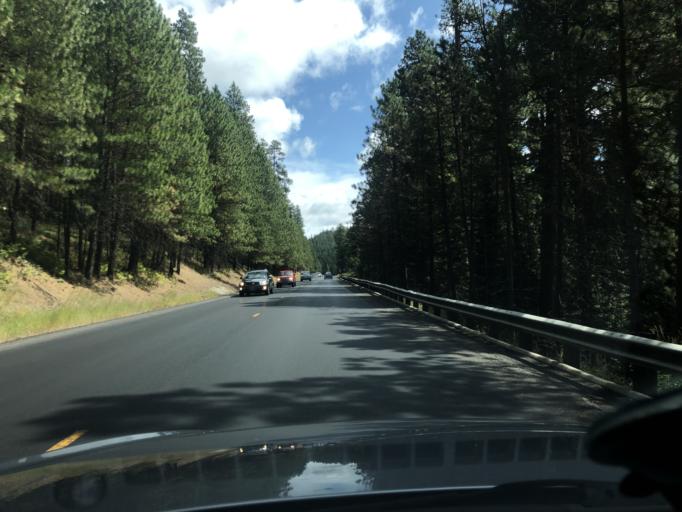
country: US
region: Washington
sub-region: Chelan County
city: Leavenworth
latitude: 47.3292
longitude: -120.6571
